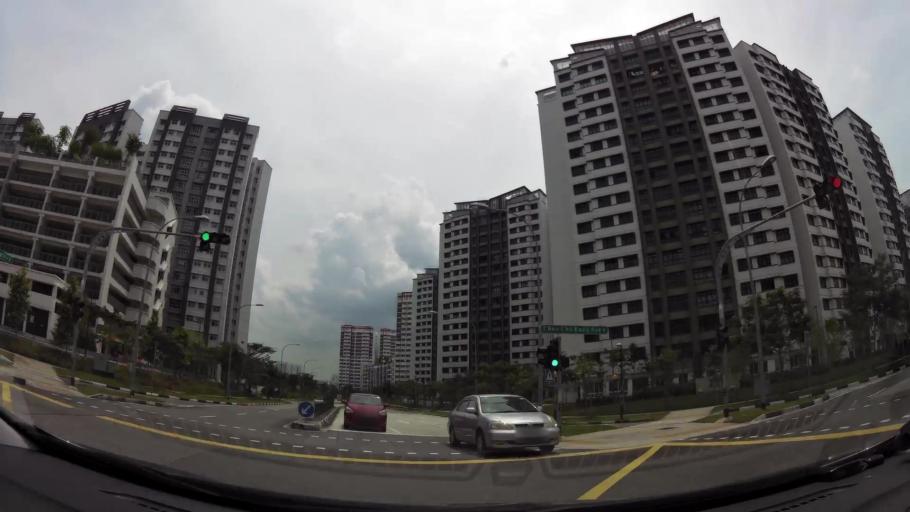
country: MY
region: Johor
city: Johor Bahru
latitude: 1.3769
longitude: 103.7460
